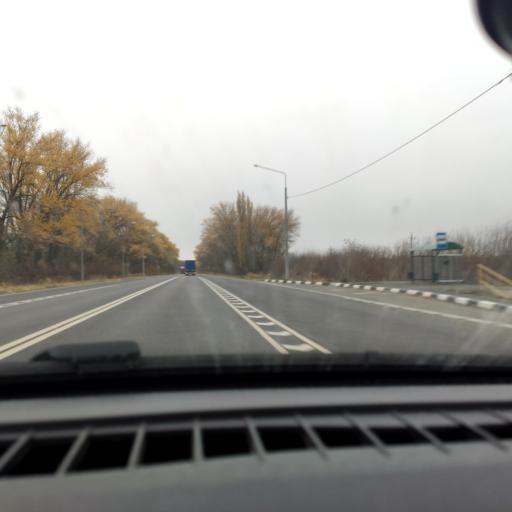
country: RU
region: Voronezj
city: Uryv-Pokrovka
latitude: 51.1734
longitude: 39.0769
